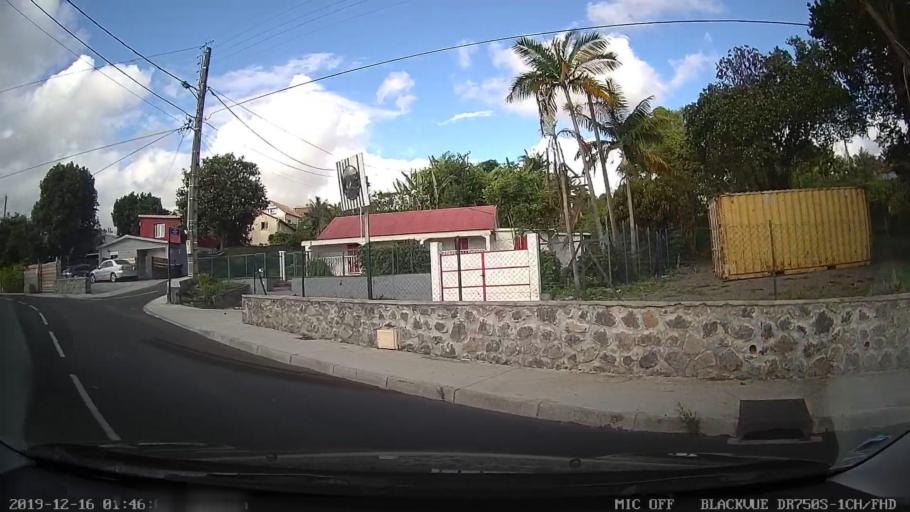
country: RE
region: Reunion
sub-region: Reunion
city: Le Tampon
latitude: -21.2484
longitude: 55.5188
